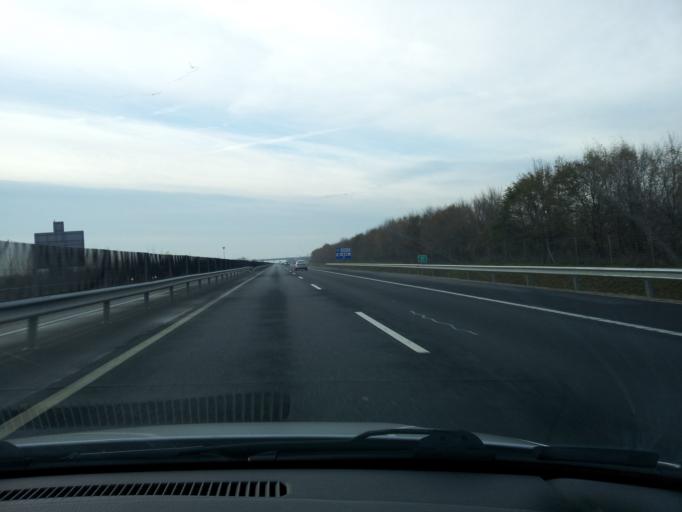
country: HU
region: Fejer
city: Rackeresztur
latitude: 47.2912
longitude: 18.8642
